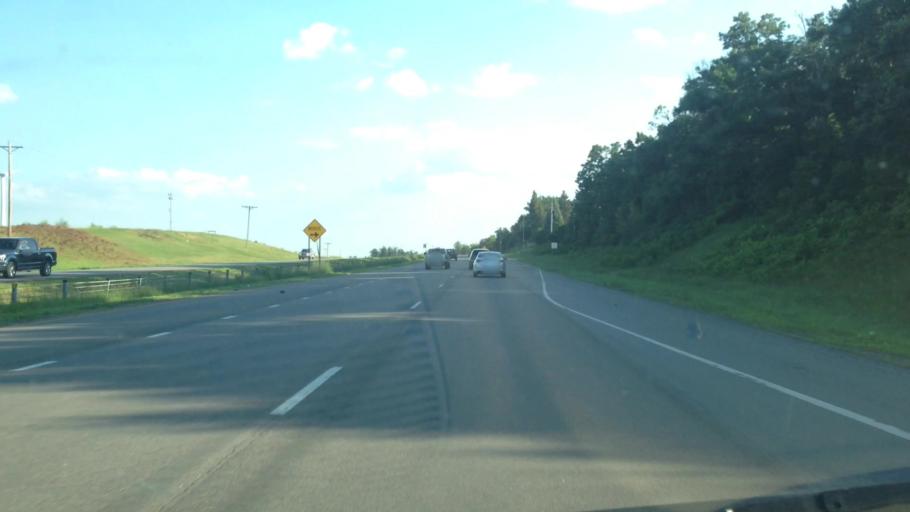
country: US
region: Minnesota
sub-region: Sherburne County
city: Zimmerman
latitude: 45.3860
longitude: -93.5634
